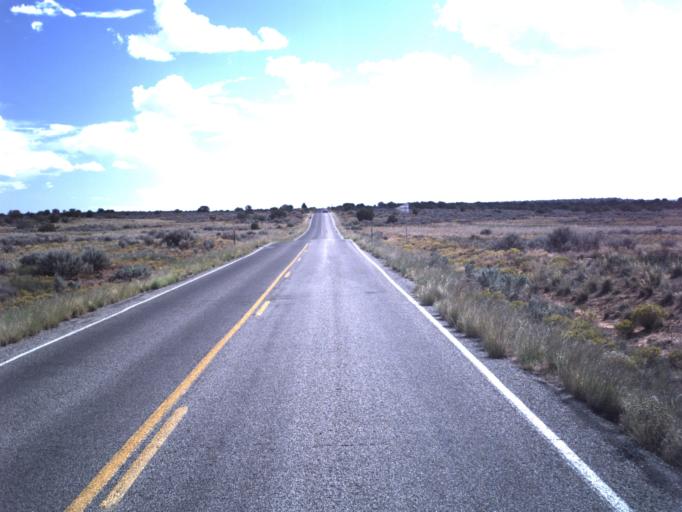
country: US
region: Utah
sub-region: Grand County
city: Moab
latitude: 38.5095
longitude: -109.7296
